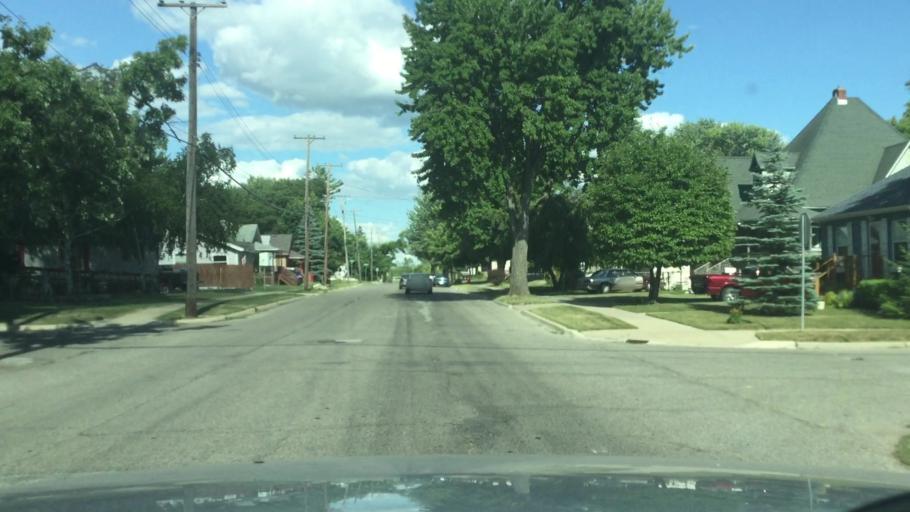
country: US
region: Michigan
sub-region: Saginaw County
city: Saginaw
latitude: 43.4006
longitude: -83.9822
